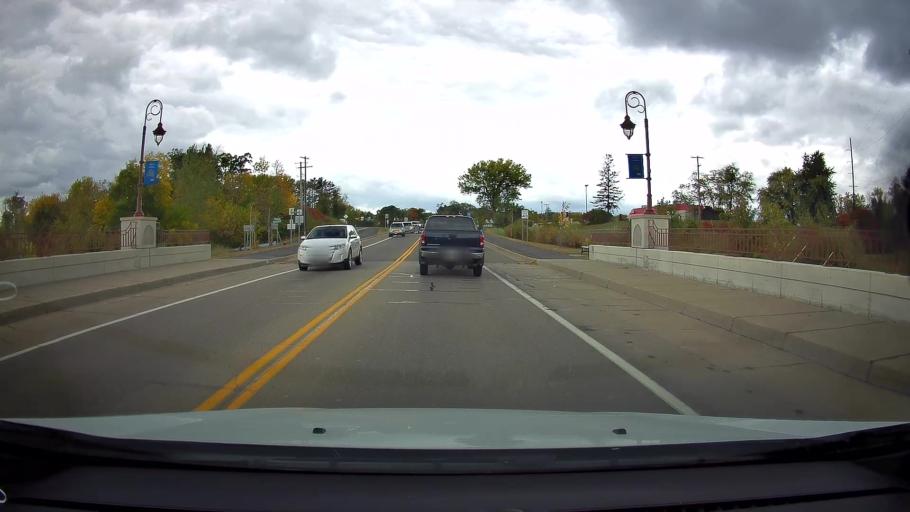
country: US
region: Minnesota
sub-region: Chisago County
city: Lindstrom
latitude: 45.3908
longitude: -92.8532
